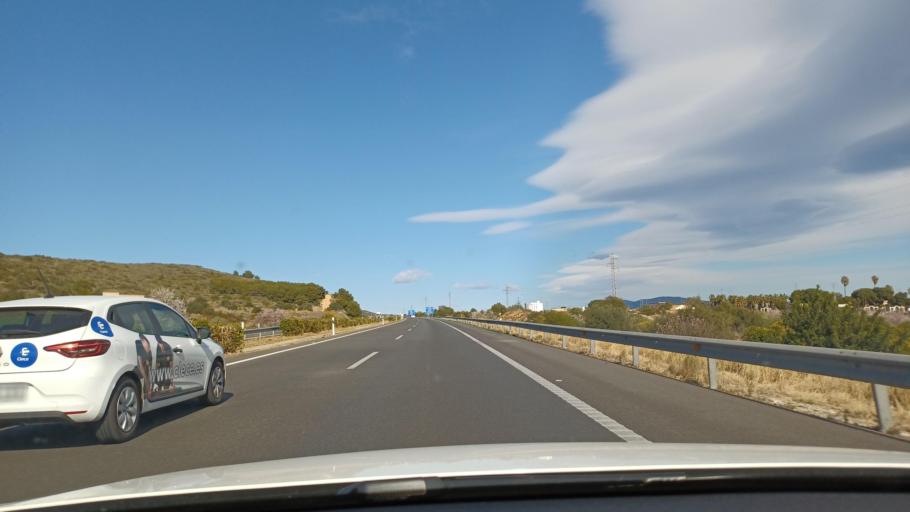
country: ES
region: Valencia
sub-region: Provincia de Castello
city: Torreblanca
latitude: 40.1877
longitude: 0.1704
